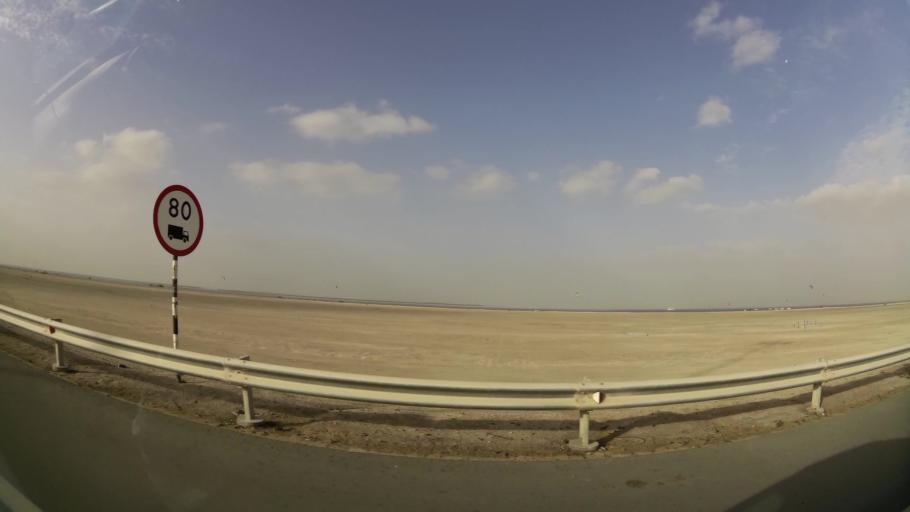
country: AE
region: Abu Dhabi
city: Abu Dhabi
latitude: 24.5072
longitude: 54.5620
